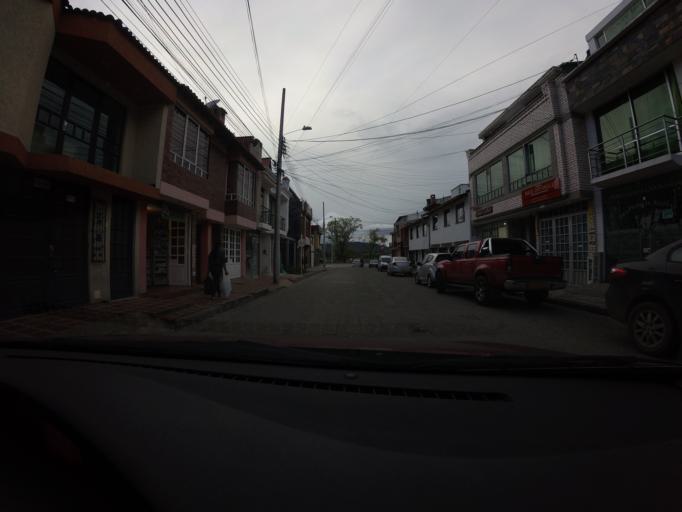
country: CO
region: Cundinamarca
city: Sopo
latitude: 4.9089
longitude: -73.9425
